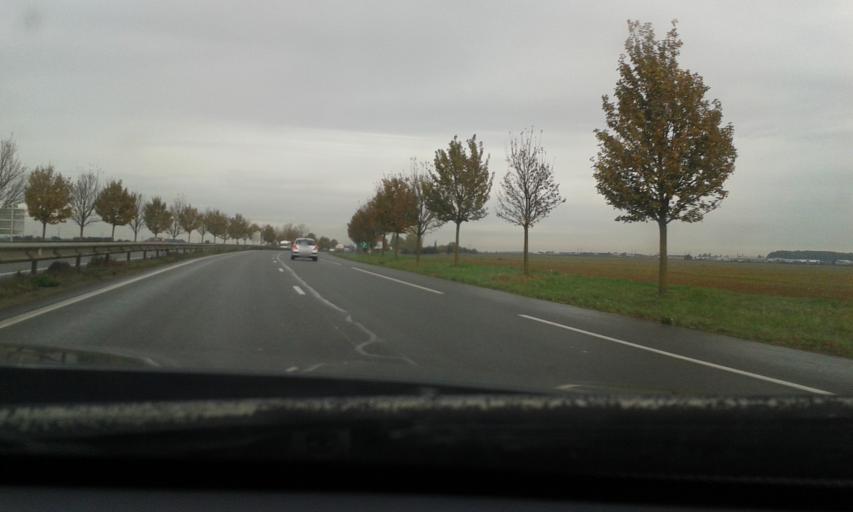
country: FR
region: Centre
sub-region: Departement d'Eure-et-Loir
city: Mainvilliers
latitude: 48.4310
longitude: 1.4315
